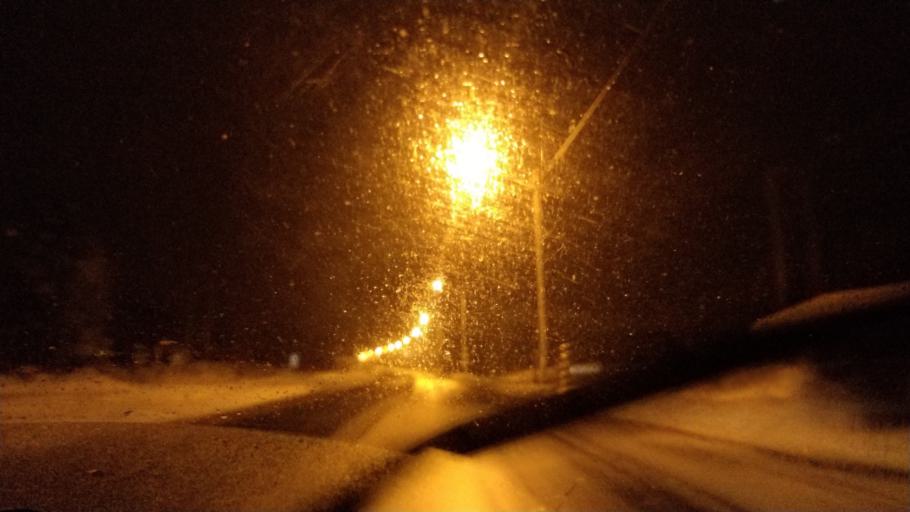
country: FI
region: Lapland
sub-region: Kemi-Tornio
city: Tervola
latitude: 66.1425
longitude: 24.9526
